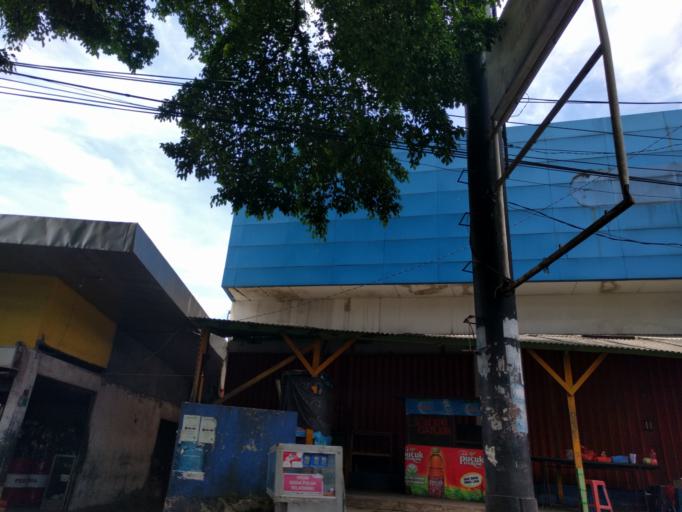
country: ID
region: West Java
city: Bogor
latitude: -6.6024
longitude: 106.8019
